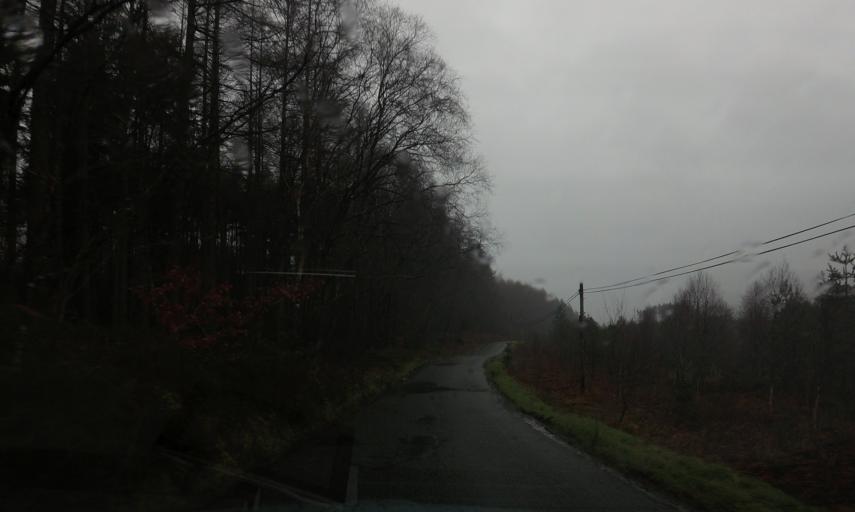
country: GB
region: Scotland
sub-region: West Dunbartonshire
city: Balloch
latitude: 56.1430
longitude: -4.6361
